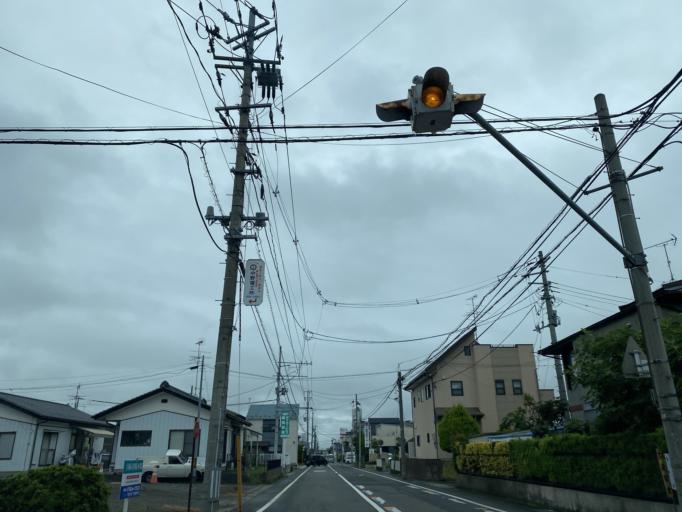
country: JP
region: Fukushima
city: Koriyama
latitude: 37.3924
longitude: 140.3265
